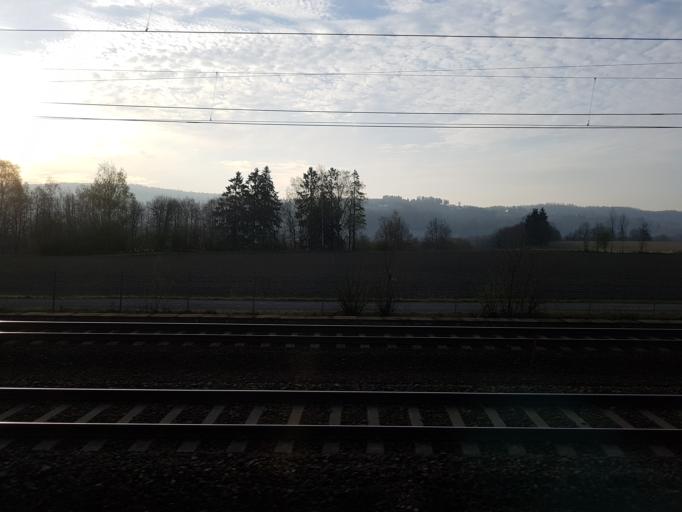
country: NO
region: Akershus
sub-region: Skedsmo
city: Leirsund
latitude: 59.9895
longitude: 11.0788
